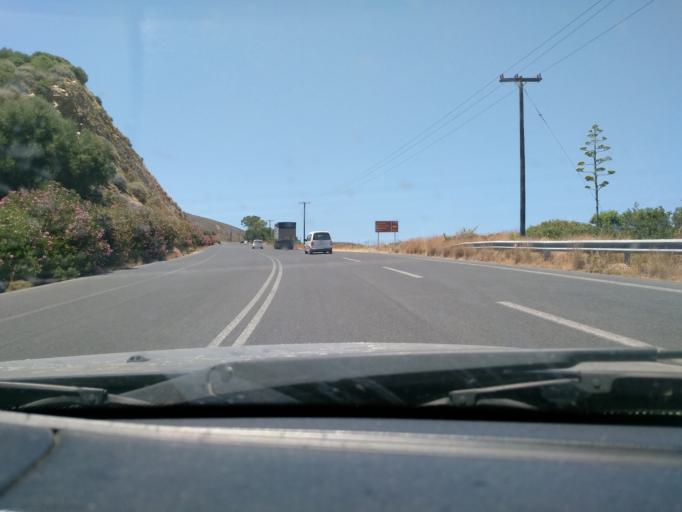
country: GR
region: Crete
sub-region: Nomos Rethymnis
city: Perama
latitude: 35.4087
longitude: 24.7741
